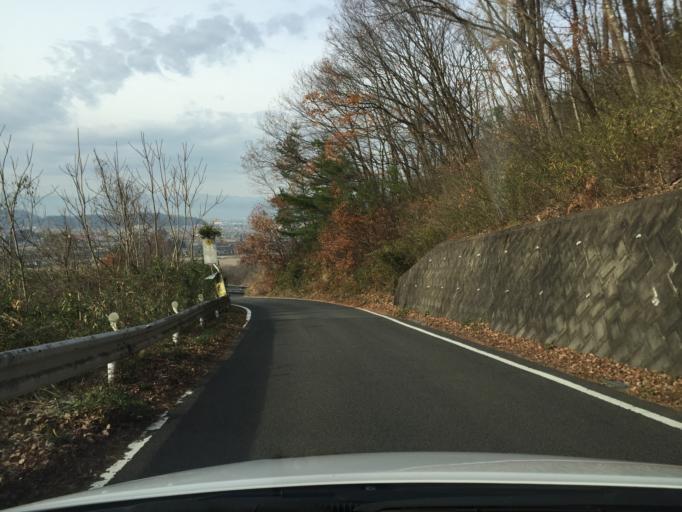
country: JP
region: Fukushima
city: Fukushima-shi
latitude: 37.7054
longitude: 140.4599
